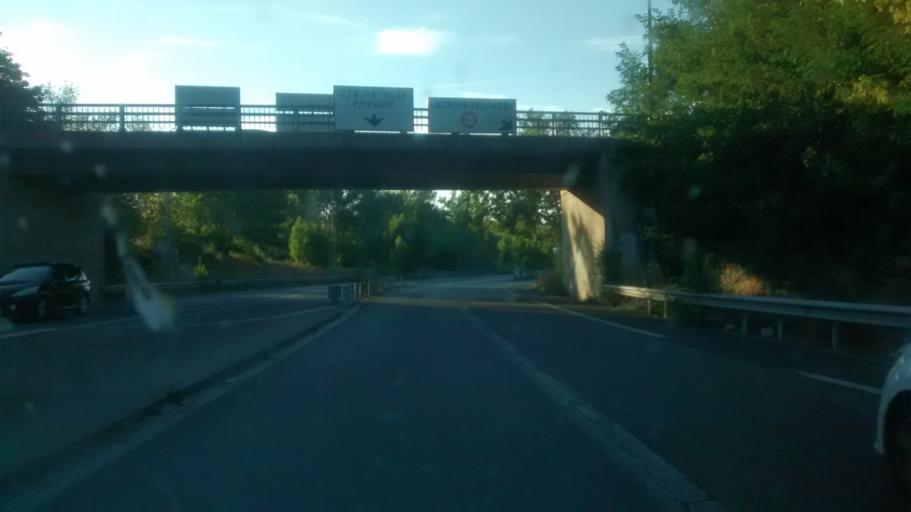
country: FR
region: Midi-Pyrenees
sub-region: Departement de la Haute-Garonne
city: Toulouse
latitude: 43.5743
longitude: 1.4377
